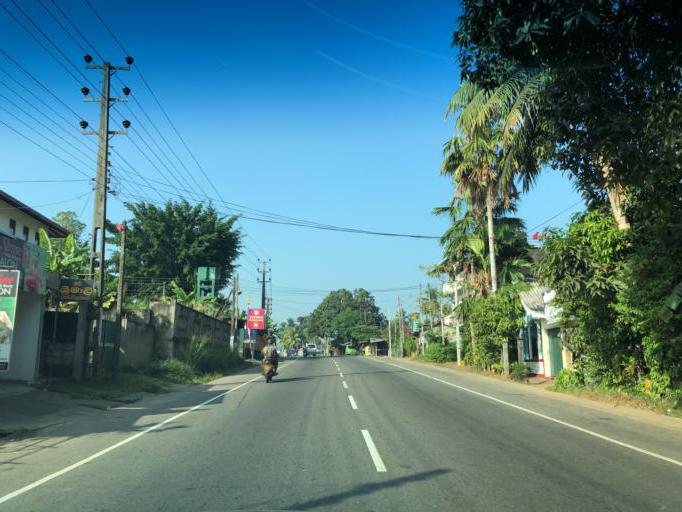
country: LK
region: Western
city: Horana South
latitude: 6.7209
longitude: 80.0739
